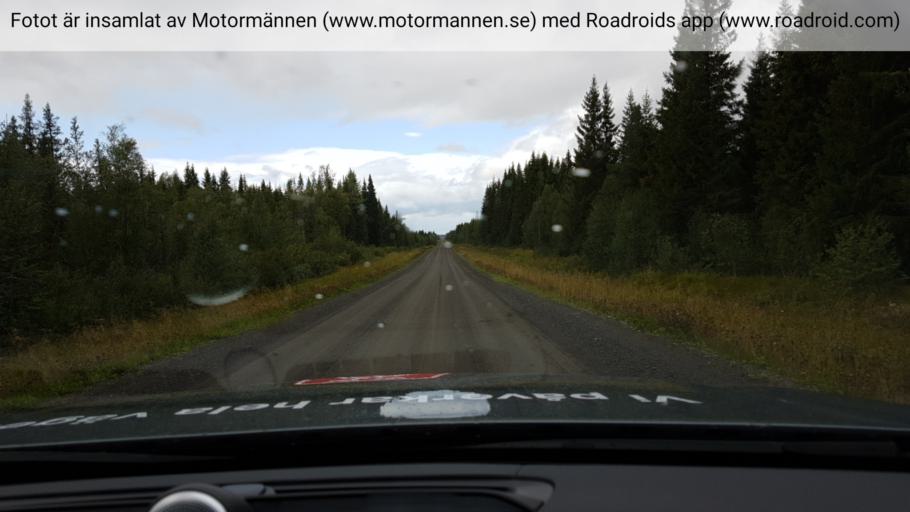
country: SE
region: Jaemtland
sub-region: OEstersunds Kommun
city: Lit
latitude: 63.6632
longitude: 14.9062
